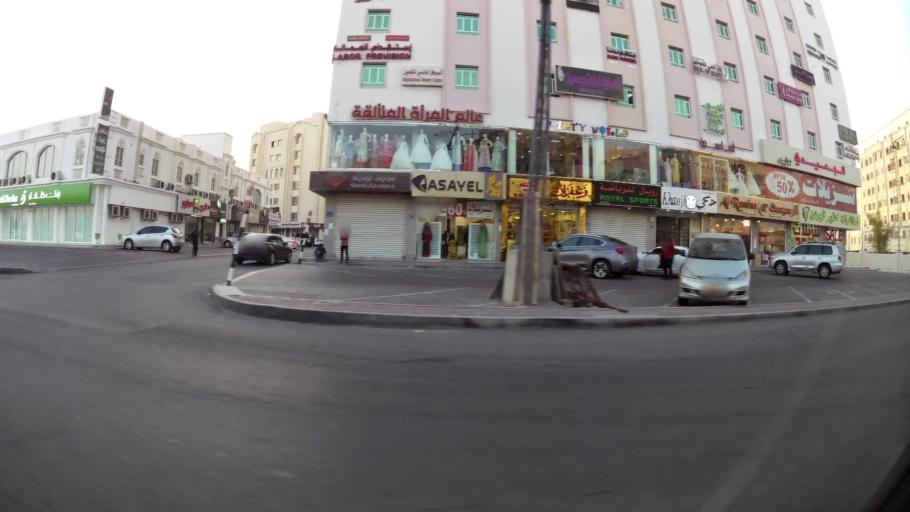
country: OM
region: Muhafazat Masqat
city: As Sib al Jadidah
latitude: 23.6404
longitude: 58.2043
